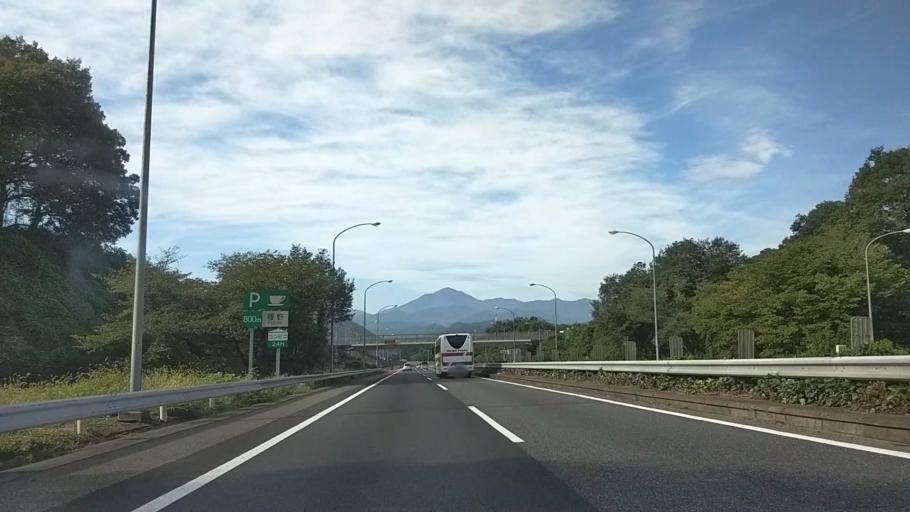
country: JP
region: Yamanashi
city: Uenohara
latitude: 35.6211
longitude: 139.1673
